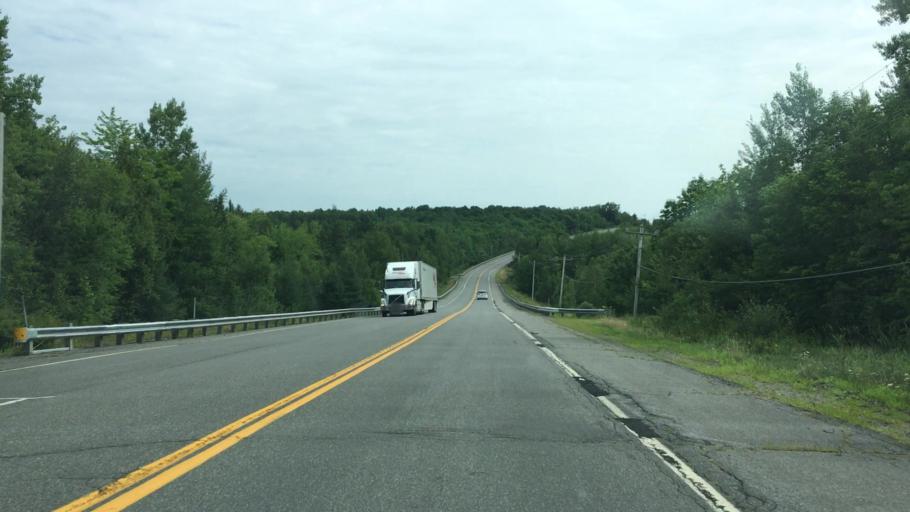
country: US
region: Maine
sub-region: Washington County
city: Calais
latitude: 45.0901
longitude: -67.4901
